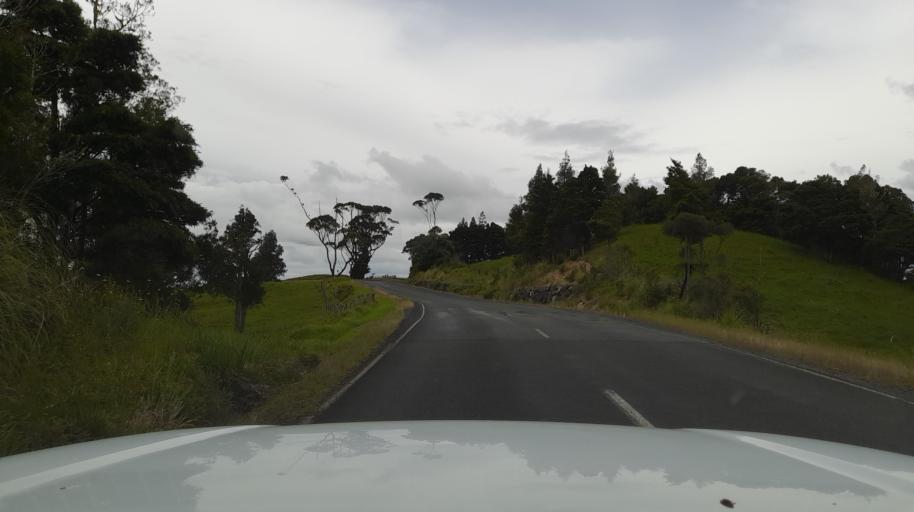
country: NZ
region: Northland
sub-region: Far North District
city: Kaitaia
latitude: -35.2783
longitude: 173.3702
